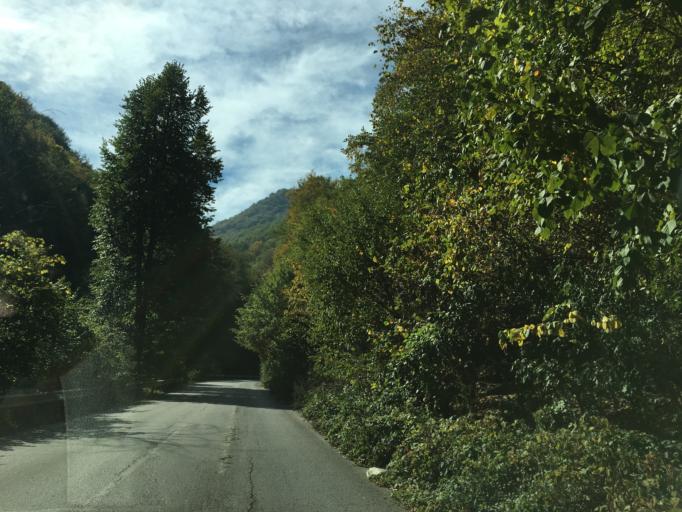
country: BG
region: Pazardzhik
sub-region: Obshtina Peshtera
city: Peshtera
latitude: 41.9995
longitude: 24.2537
